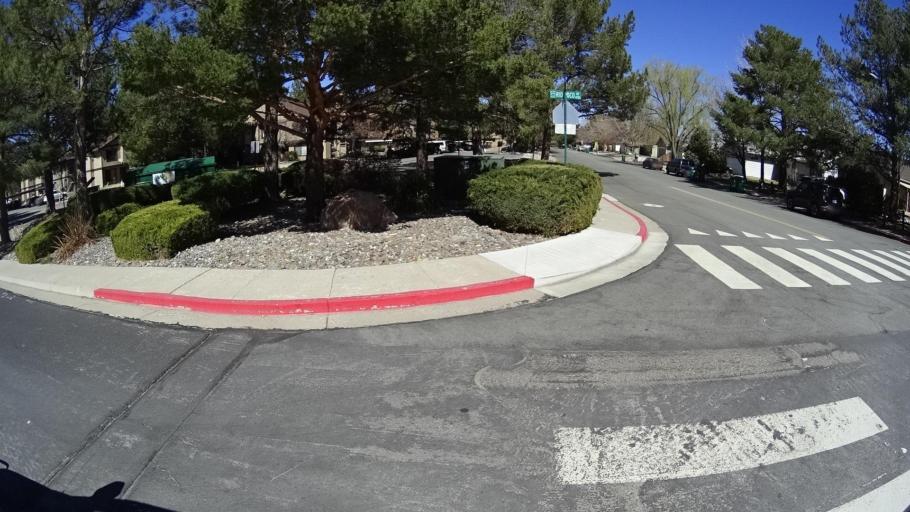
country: US
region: Nevada
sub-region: Washoe County
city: Sparks
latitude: 39.4722
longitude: -119.7481
